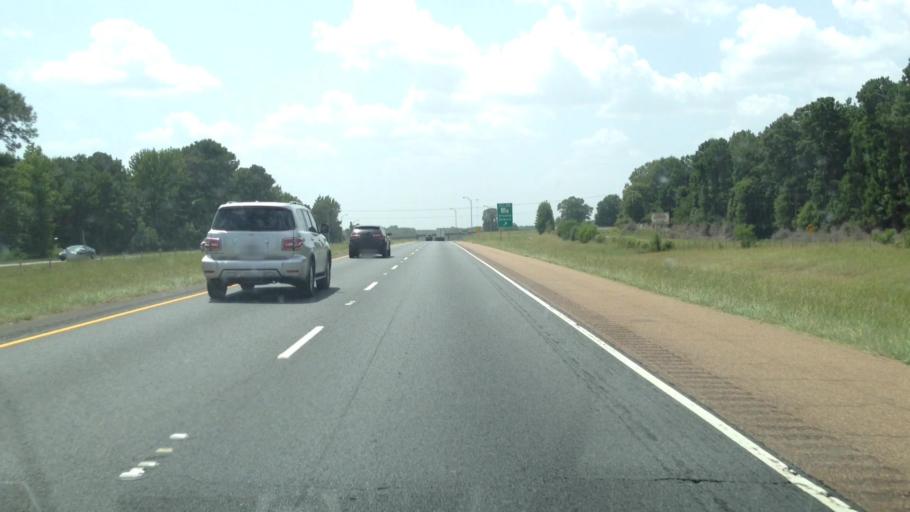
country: US
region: Louisiana
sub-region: Bienville Parish
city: Arcadia
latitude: 32.5622
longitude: -92.9031
